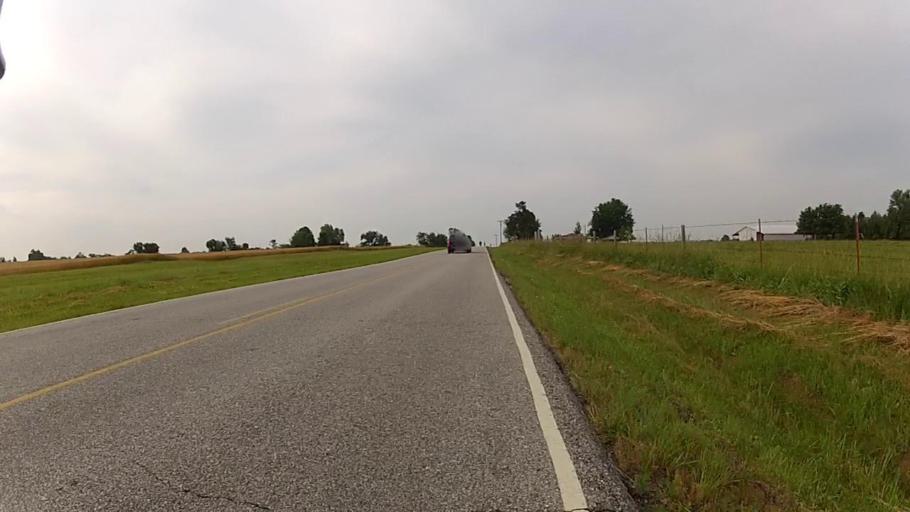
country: US
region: Kansas
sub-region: Cherokee County
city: Baxter Springs
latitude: 37.0811
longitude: -94.7227
